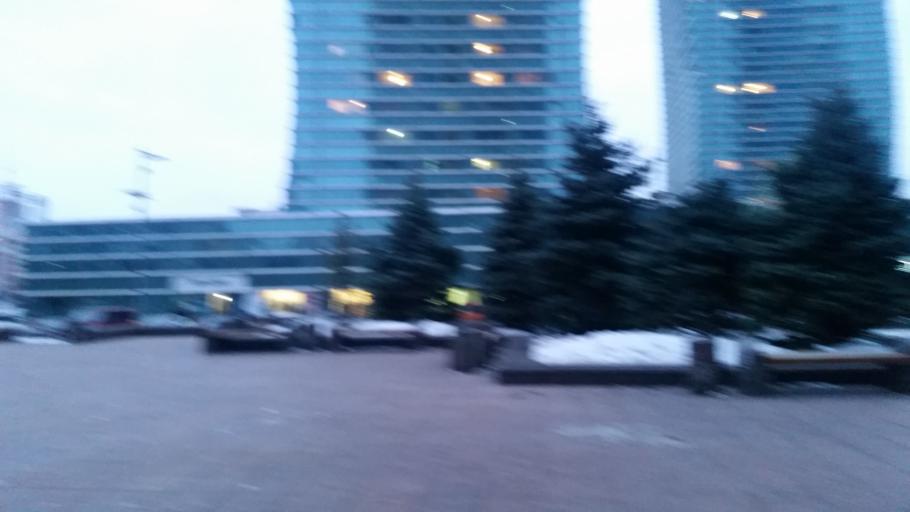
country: KZ
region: Astana Qalasy
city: Astana
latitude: 51.1294
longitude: 71.4227
